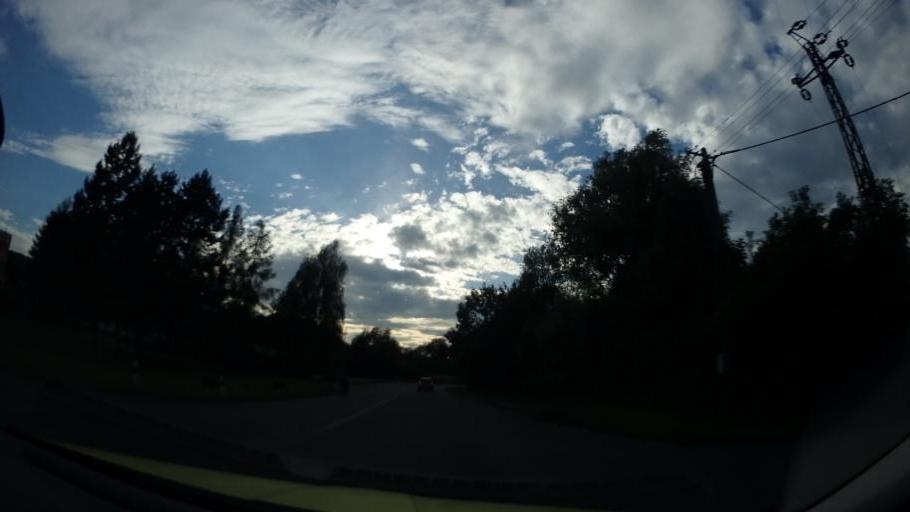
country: CZ
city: Rybi
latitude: 49.5952
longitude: 18.0940
